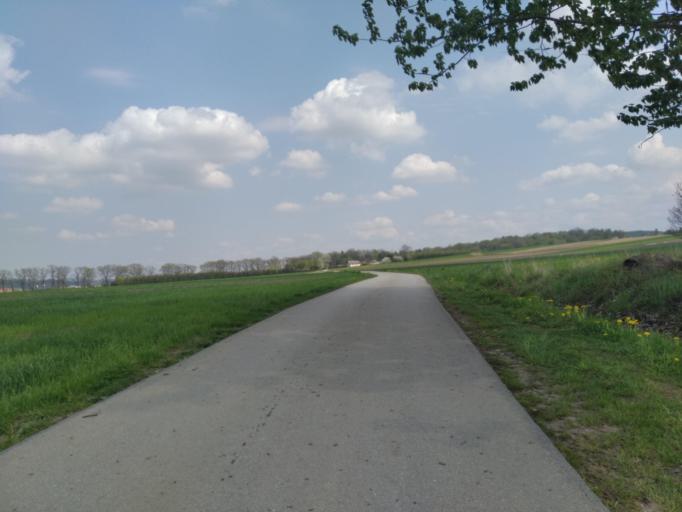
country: PL
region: Subcarpathian Voivodeship
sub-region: Powiat brzozowski
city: Jasionow
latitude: 49.6442
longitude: 21.9875
